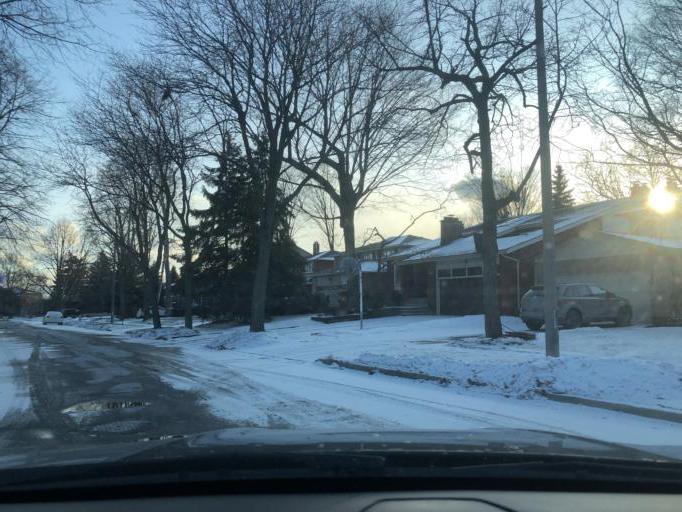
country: CA
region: Ontario
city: Scarborough
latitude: 43.7847
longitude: -79.1548
